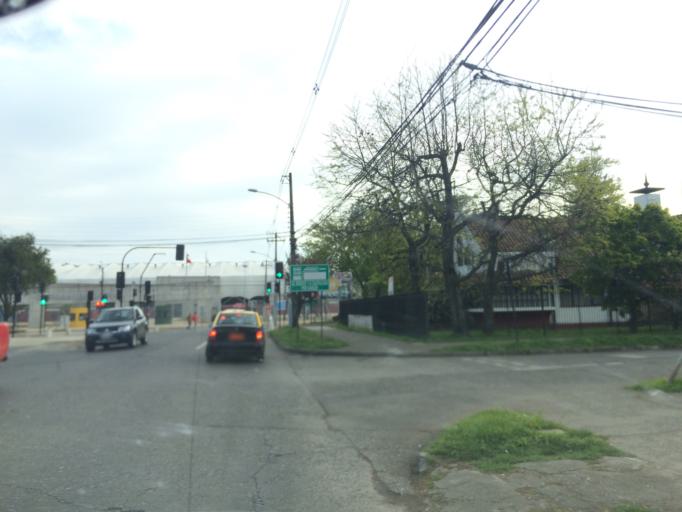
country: CL
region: Araucania
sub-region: Provincia de Cautin
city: Temuco
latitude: -38.7403
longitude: -72.6187
